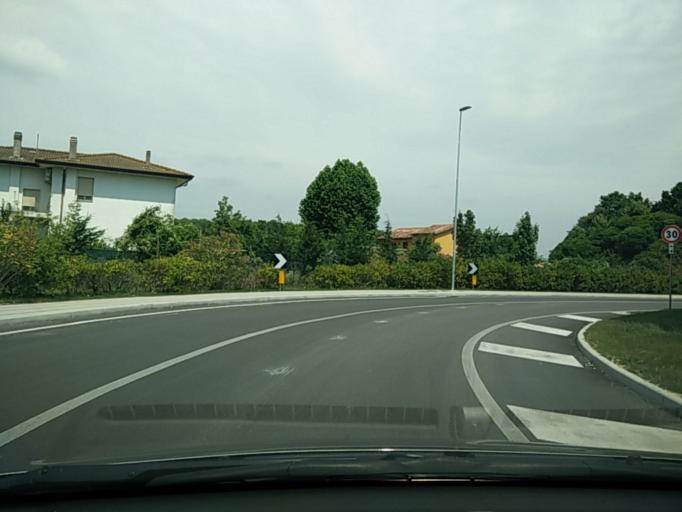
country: IT
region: Veneto
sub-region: Provincia di Venezia
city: Tessera
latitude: 45.5086
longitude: 12.3373
